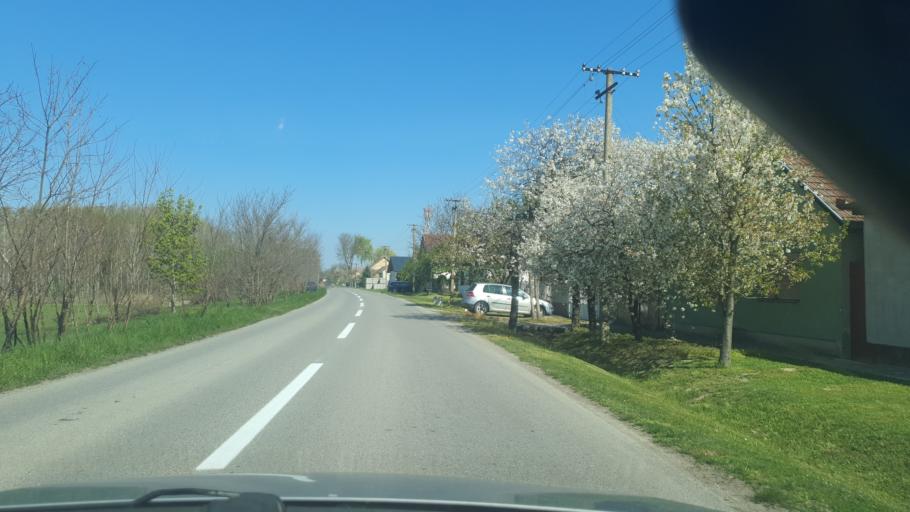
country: RS
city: Kolut
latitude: 45.8809
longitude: 18.9341
